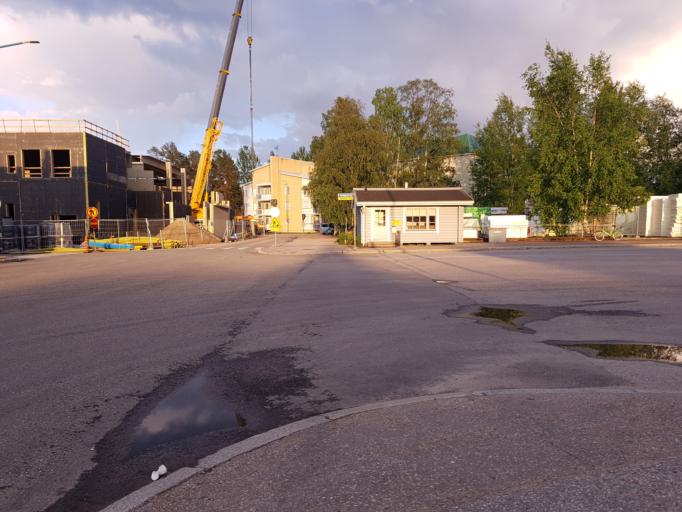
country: FI
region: Kainuu
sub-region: Kajaani
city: Kajaani
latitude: 64.2221
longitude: 27.7301
